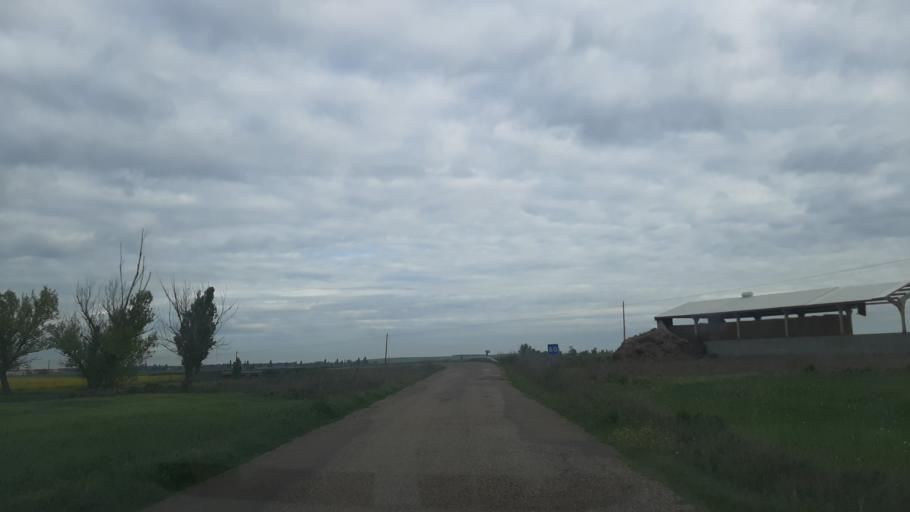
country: ES
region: Castille and Leon
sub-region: Provincia de Salamanca
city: Villaflores
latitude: 41.0797
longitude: -5.2196
